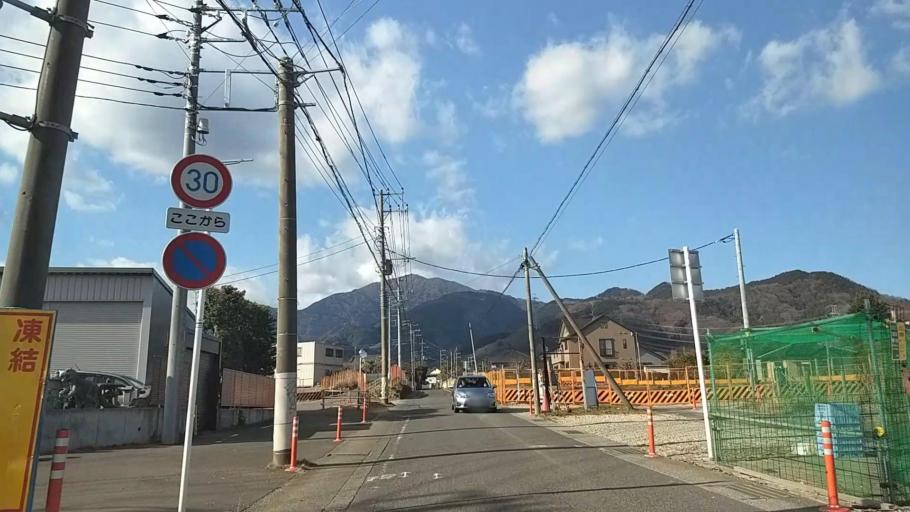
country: JP
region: Kanagawa
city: Isehara
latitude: 35.4116
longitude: 139.2875
